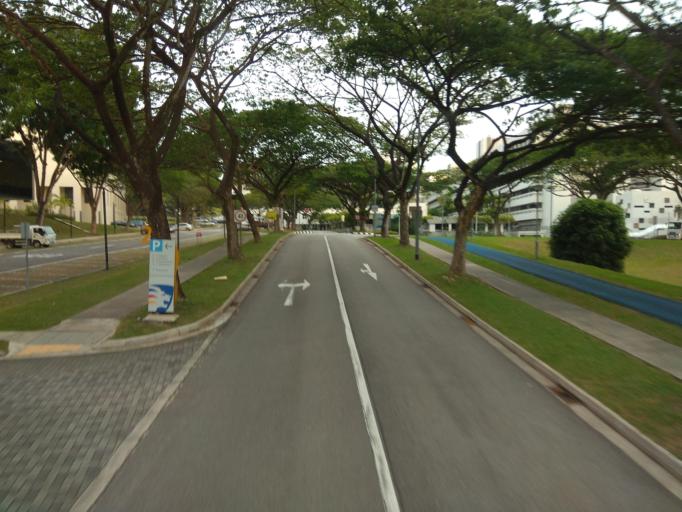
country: MY
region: Johor
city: Johor Bahru
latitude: 1.3471
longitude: 103.6777
